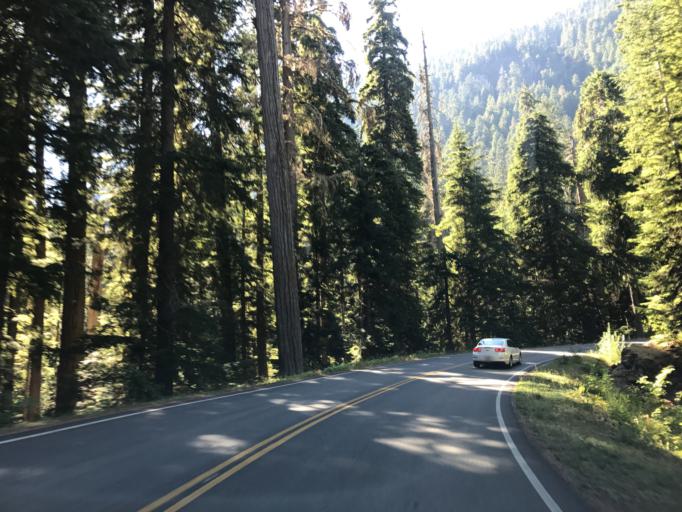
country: US
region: Washington
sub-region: Pierce County
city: Buckley
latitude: 46.7440
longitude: -121.5720
